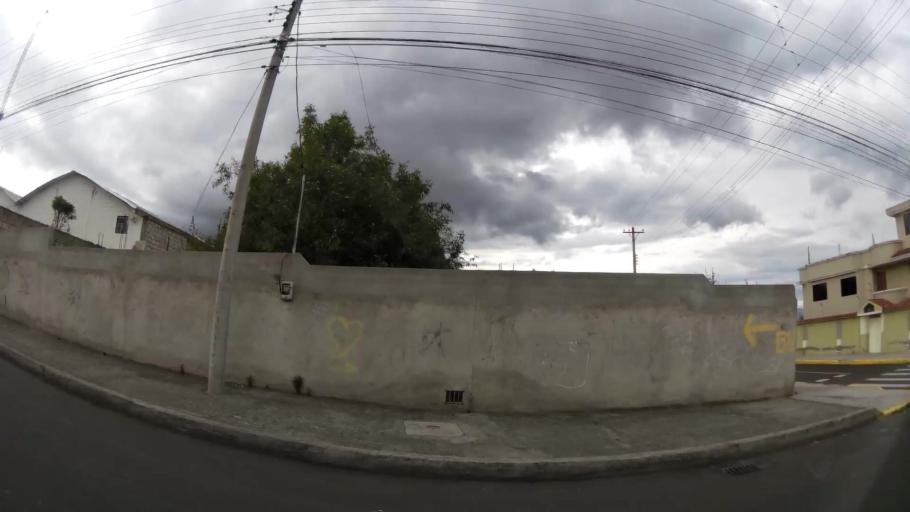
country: EC
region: Tungurahua
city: Ambato
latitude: -1.2642
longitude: -78.6161
